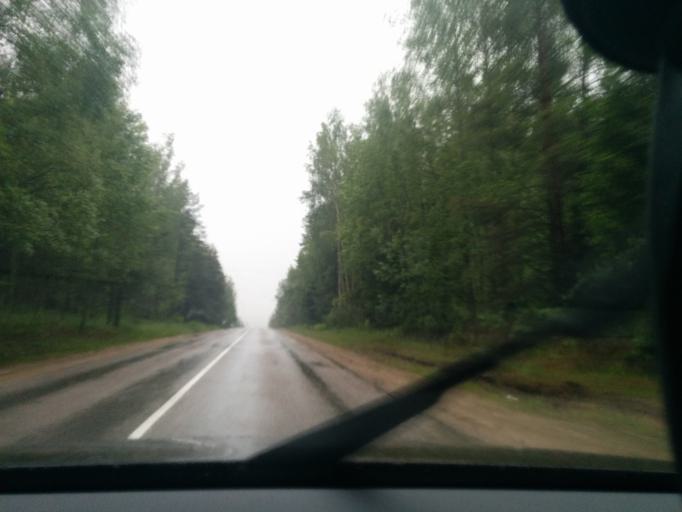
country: LV
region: Ogre
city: Ogre
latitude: 56.8451
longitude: 24.5730
